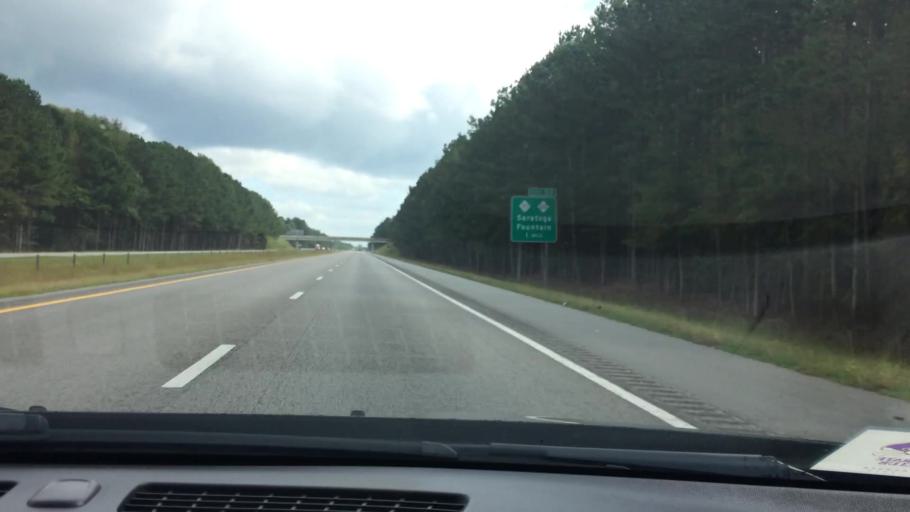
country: US
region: North Carolina
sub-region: Wilson County
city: Wilson
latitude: 35.6717
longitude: -77.7873
